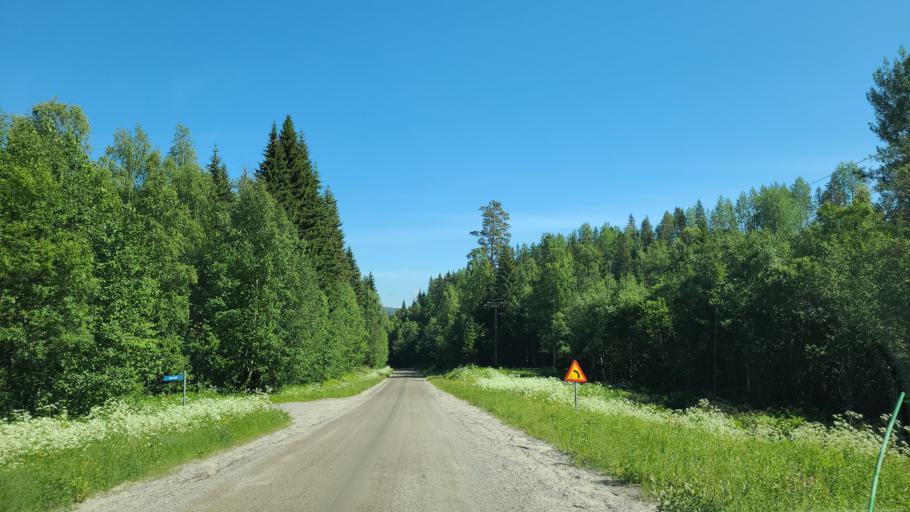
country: SE
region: Vaesterbotten
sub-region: Nordmalings Kommun
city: Nordmaling
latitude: 63.6469
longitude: 19.2316
